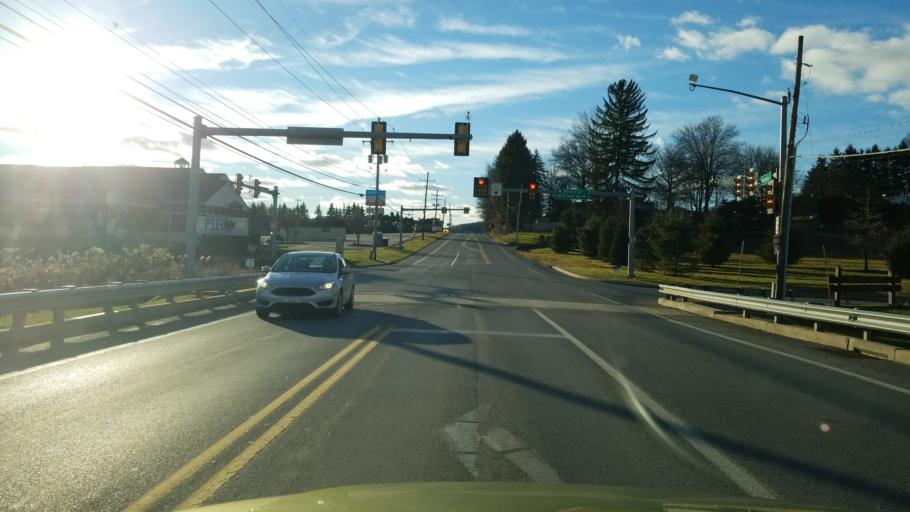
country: US
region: Pennsylvania
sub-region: Indiana County
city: Indiana
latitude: 40.6224
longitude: -79.1887
